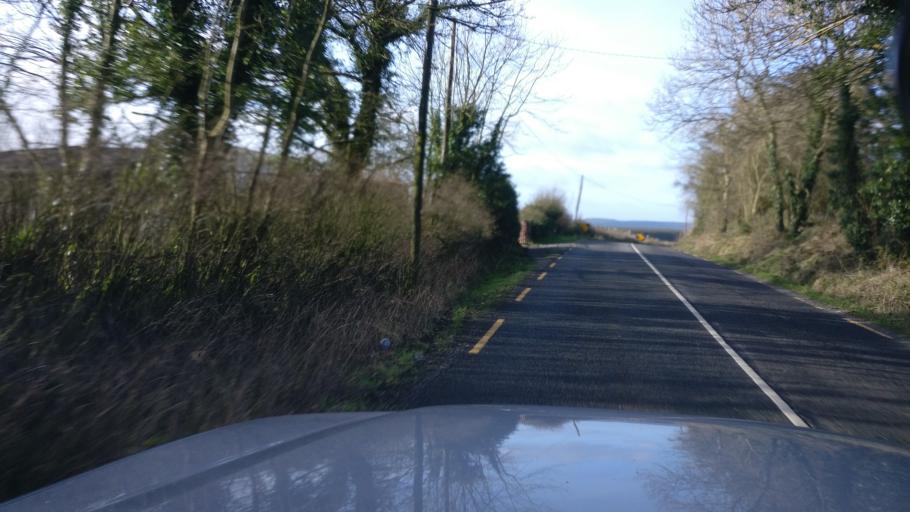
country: IE
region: Leinster
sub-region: Laois
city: Stradbally
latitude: 52.9224
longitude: -7.1921
